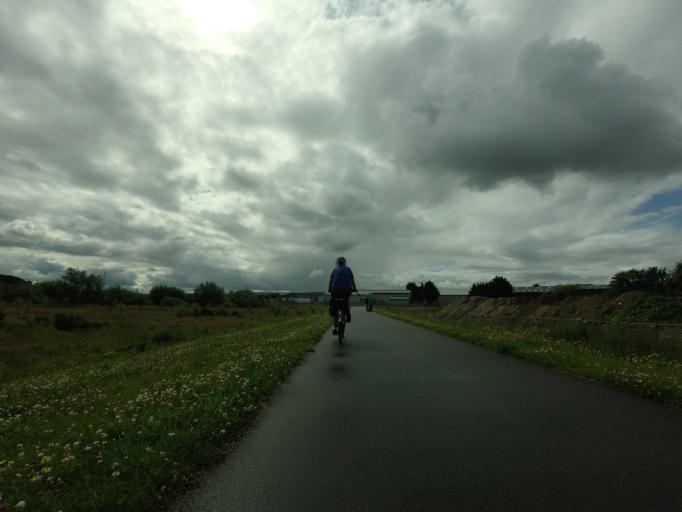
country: GB
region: Scotland
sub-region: Moray
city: Elgin
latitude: 57.6489
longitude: -3.2844
